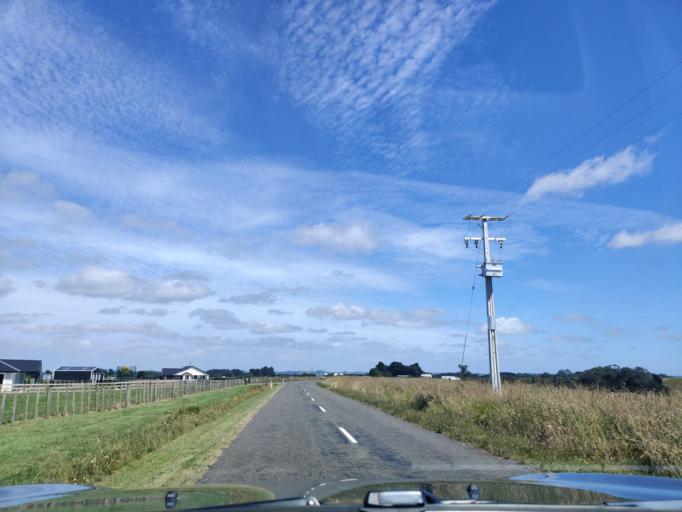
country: NZ
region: Manawatu-Wanganui
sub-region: Rangitikei District
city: Bulls
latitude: -40.1856
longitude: 175.4464
